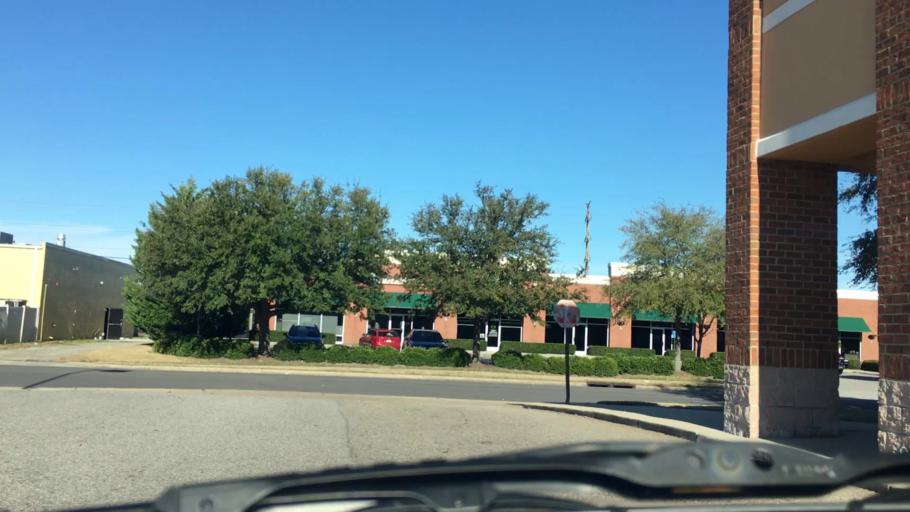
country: US
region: Virginia
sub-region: City of Virginia Beach
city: Virginia Beach
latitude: 36.8488
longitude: -76.0189
